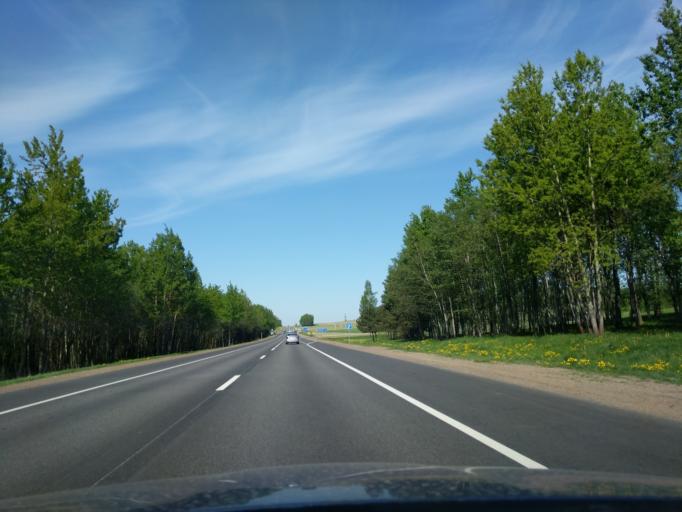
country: BY
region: Minsk
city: Bal'shavik
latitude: 54.0877
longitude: 27.5438
